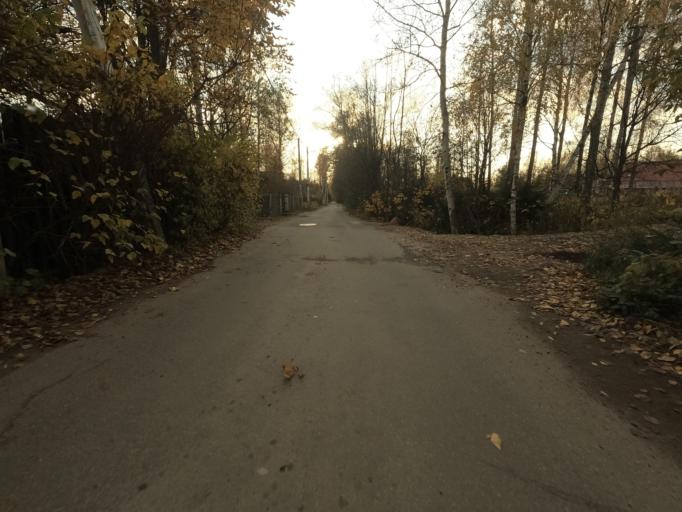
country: RU
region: St.-Petersburg
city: Beloostrov
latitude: 60.1840
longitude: 30.0545
